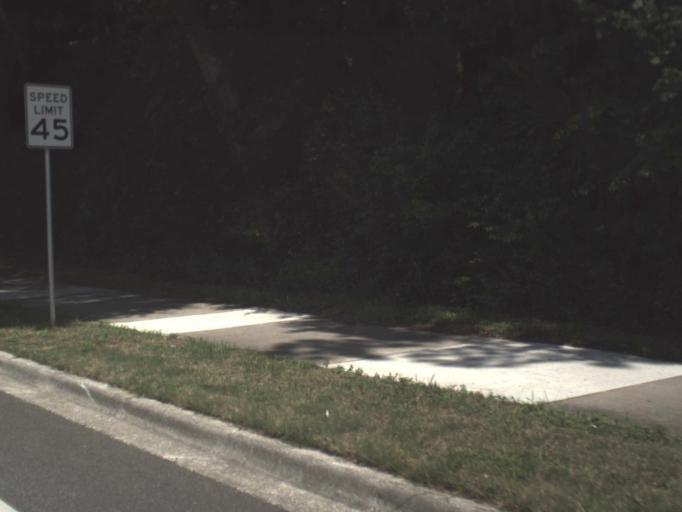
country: US
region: Florida
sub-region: Alachua County
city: Gainesville
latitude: 29.6148
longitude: -82.3427
